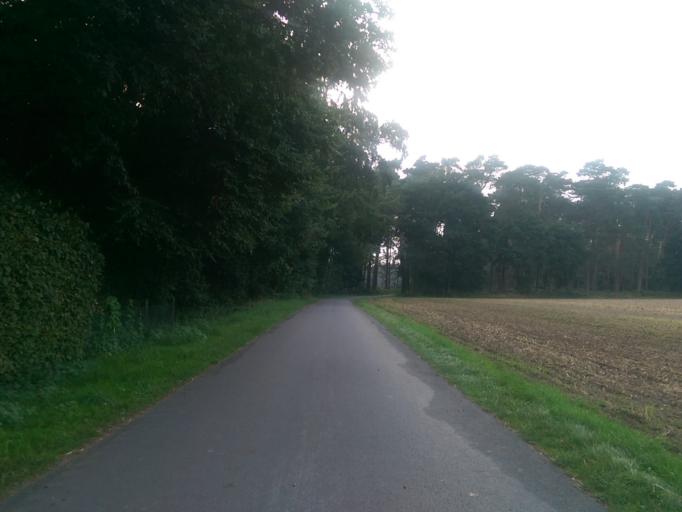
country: DE
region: North Rhine-Westphalia
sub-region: Regierungsbezirk Detmold
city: Rheda-Wiedenbruck
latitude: 51.8719
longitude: 8.3420
